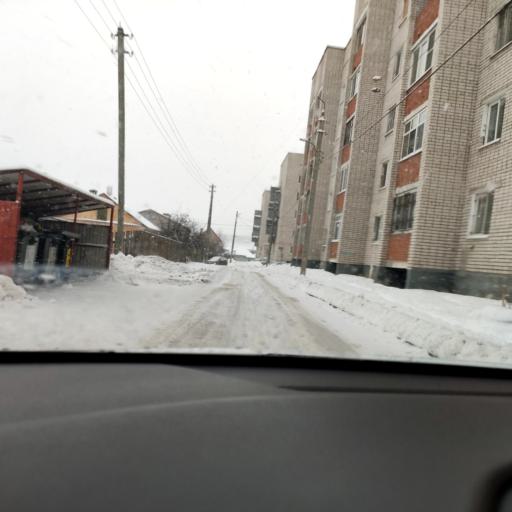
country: RU
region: Tatarstan
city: Vysokaya Gora
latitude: 55.8635
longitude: 49.2315
